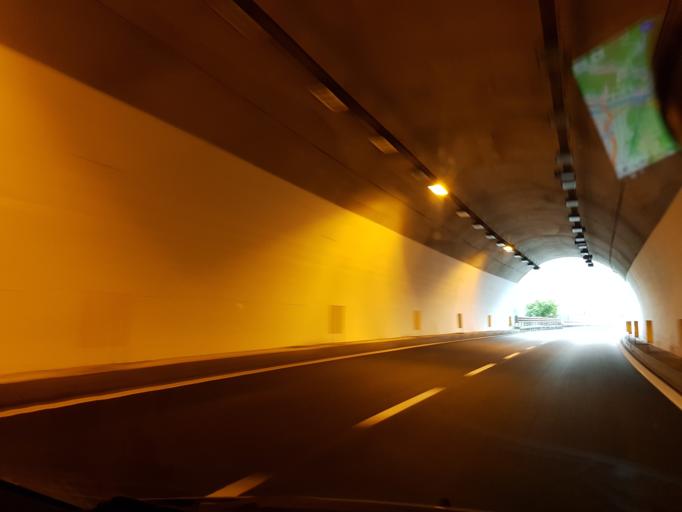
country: IT
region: Tuscany
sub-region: Provincia di Massa-Carrara
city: Aulla
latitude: 44.2081
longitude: 9.9631
